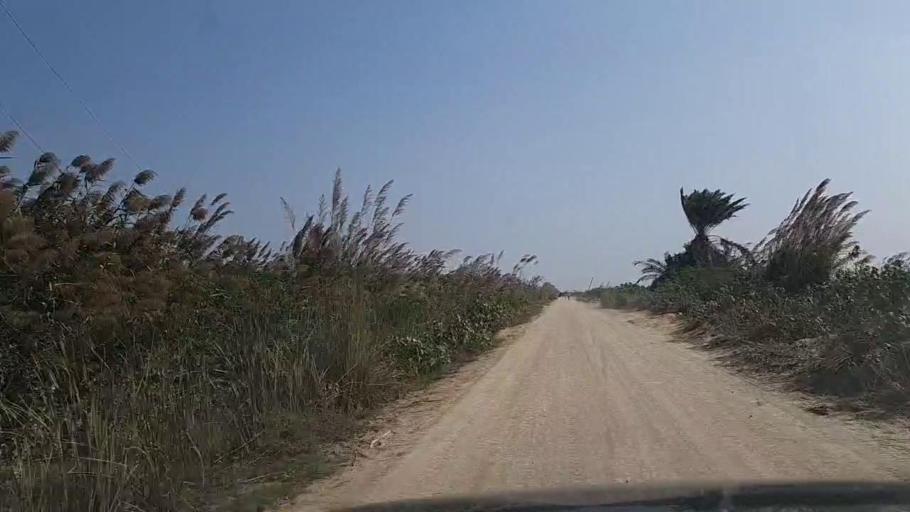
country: PK
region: Sindh
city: Gharo
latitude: 24.7194
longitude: 67.5606
